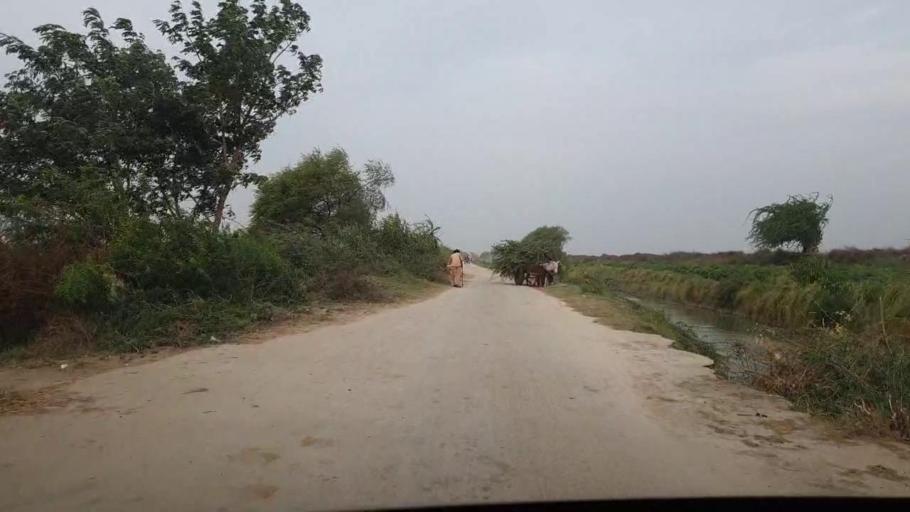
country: PK
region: Sindh
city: Chuhar Jamali
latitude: 24.4024
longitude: 67.9622
